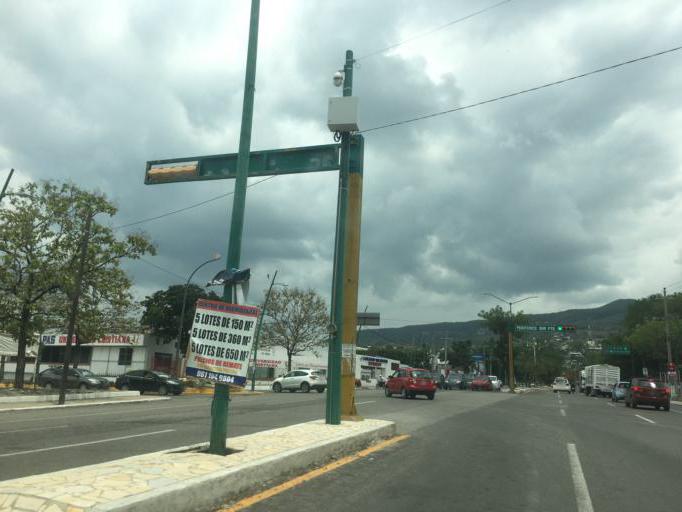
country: MX
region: Chiapas
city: Tuxtla Gutierrez
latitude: 16.7509
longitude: -93.1416
